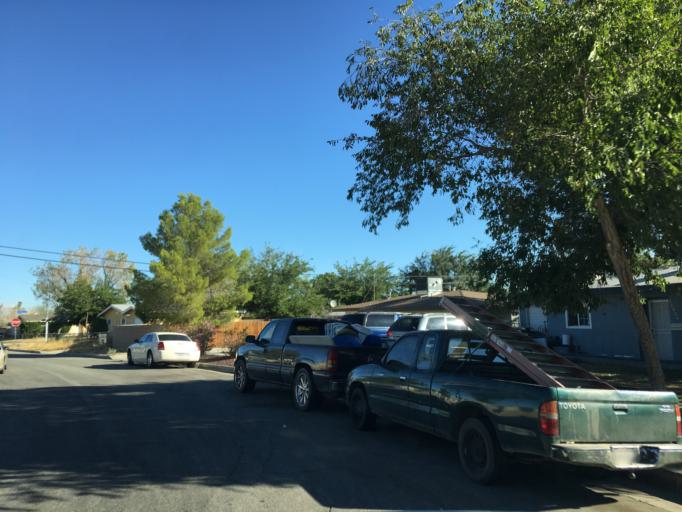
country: US
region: California
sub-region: Los Angeles County
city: Desert View Highlands
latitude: 34.5892
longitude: -118.1549
